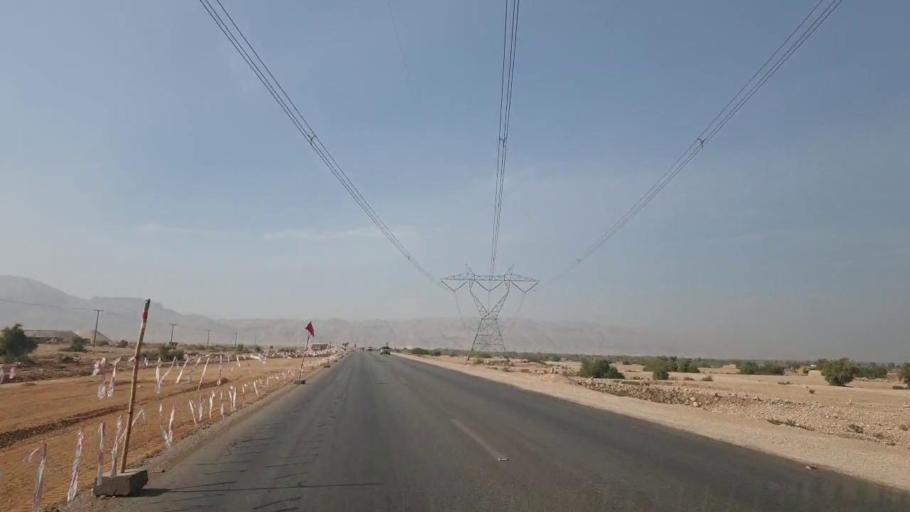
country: PK
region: Sindh
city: Sehwan
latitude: 26.2095
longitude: 67.9257
